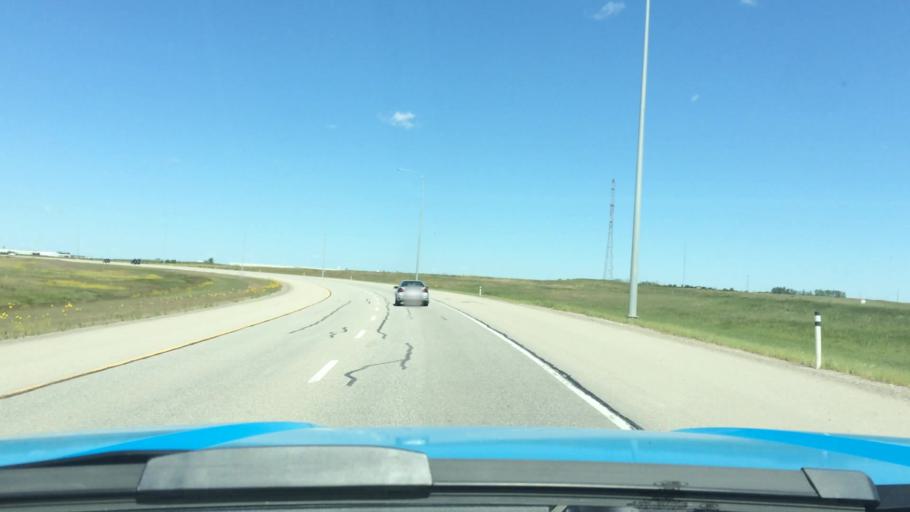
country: CA
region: Alberta
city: Chestermere
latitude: 51.1737
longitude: -113.9133
